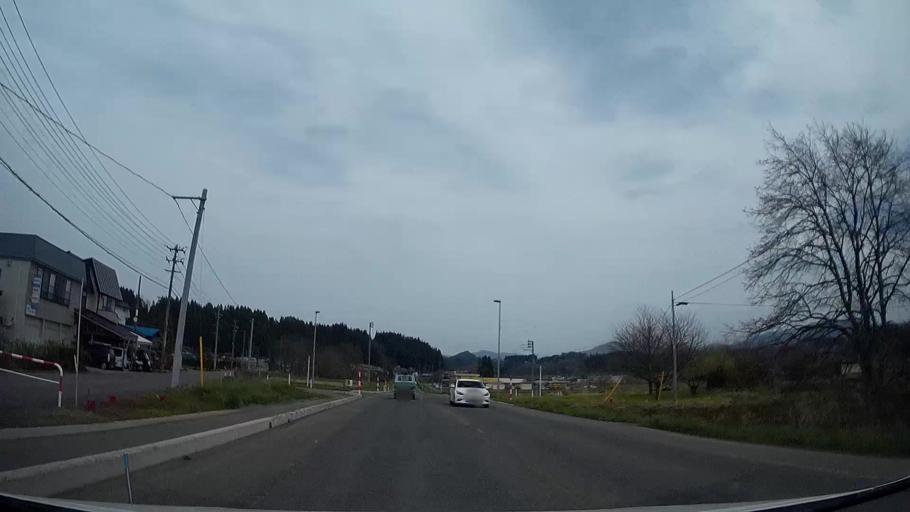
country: JP
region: Akita
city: Hanawa
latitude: 40.2720
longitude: 140.7879
